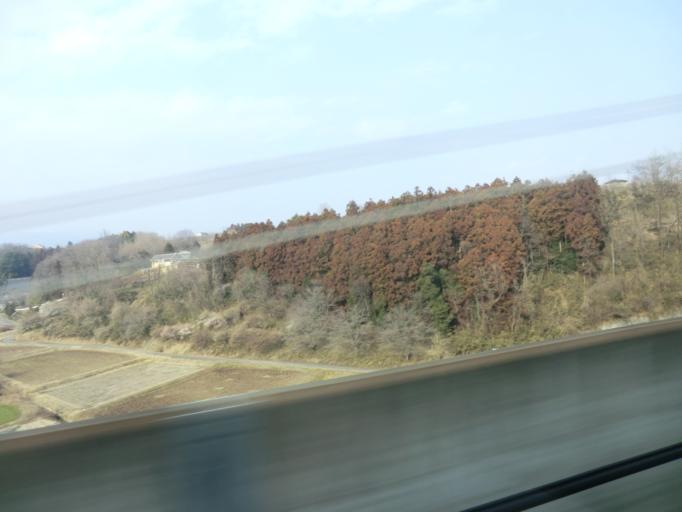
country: JP
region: Gunma
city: Kanekomachi
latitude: 36.3800
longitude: 138.9475
